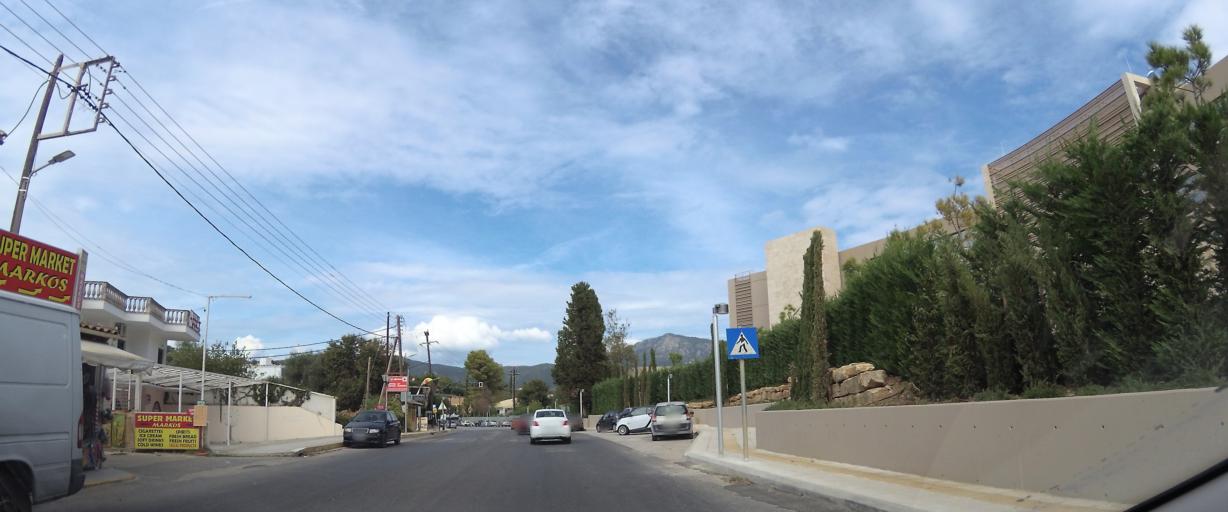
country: GR
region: Ionian Islands
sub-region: Nomos Kerkyras
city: Kontokali
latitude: 39.6797
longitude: 19.8384
